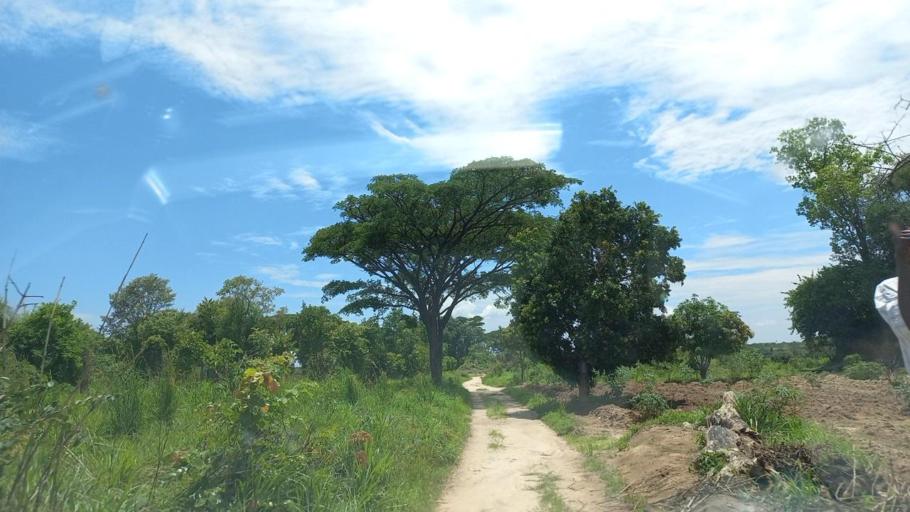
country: ZM
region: Copperbelt
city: Ndola
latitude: -12.8753
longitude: 28.4452
